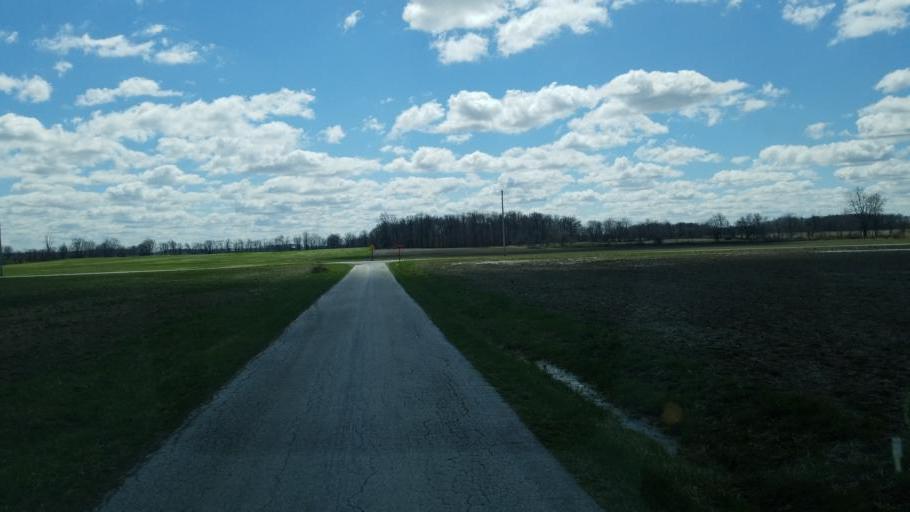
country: US
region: Ohio
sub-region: Hancock County
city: Arlington
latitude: 40.9467
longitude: -83.5229
